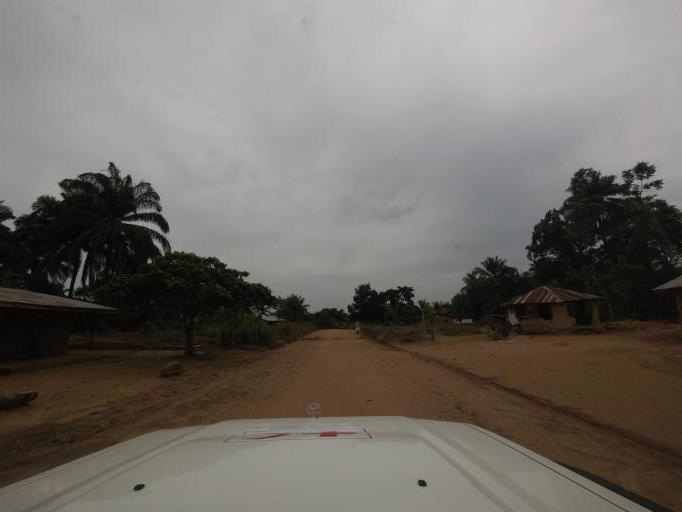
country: SL
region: Eastern Province
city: Buedu
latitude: 8.3384
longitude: -10.2076
